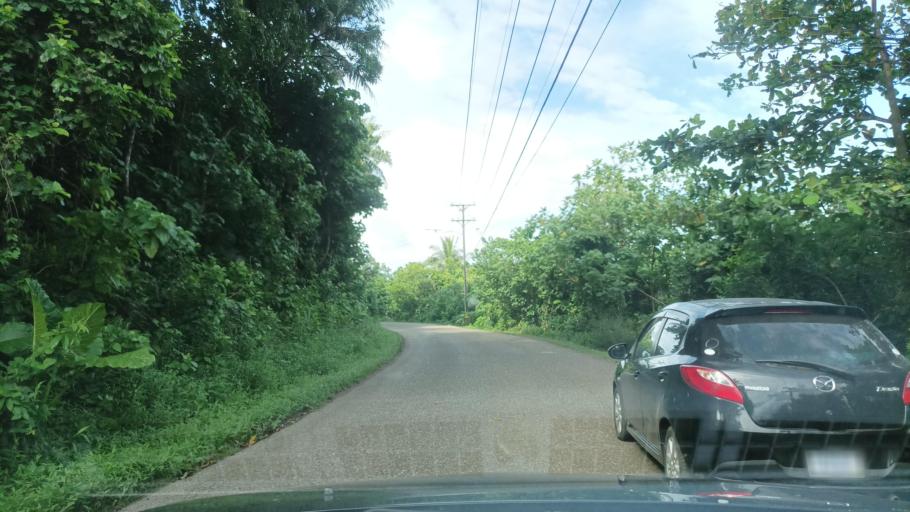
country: FM
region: Kosrae
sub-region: Lelu Municipality
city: Lelu
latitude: 5.3387
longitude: 163.0169
